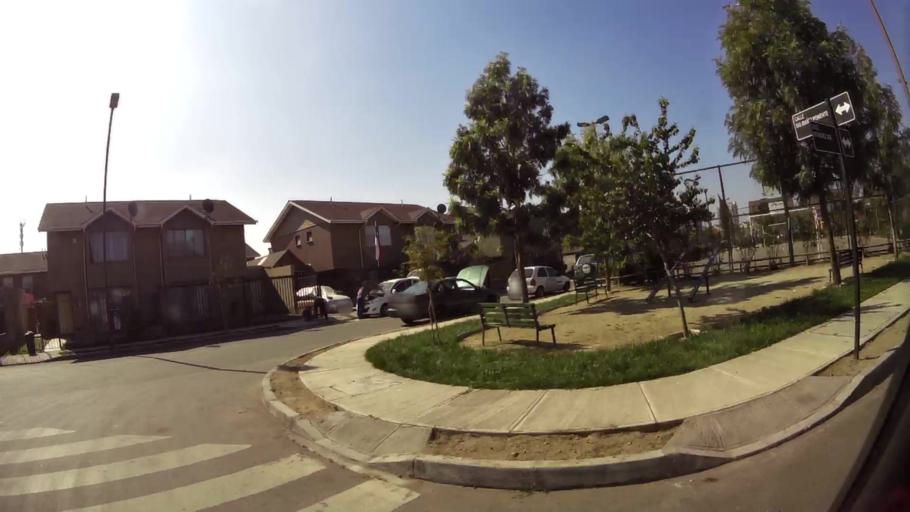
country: CL
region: Santiago Metropolitan
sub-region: Provincia de Santiago
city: Lo Prado
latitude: -33.4817
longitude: -70.7640
